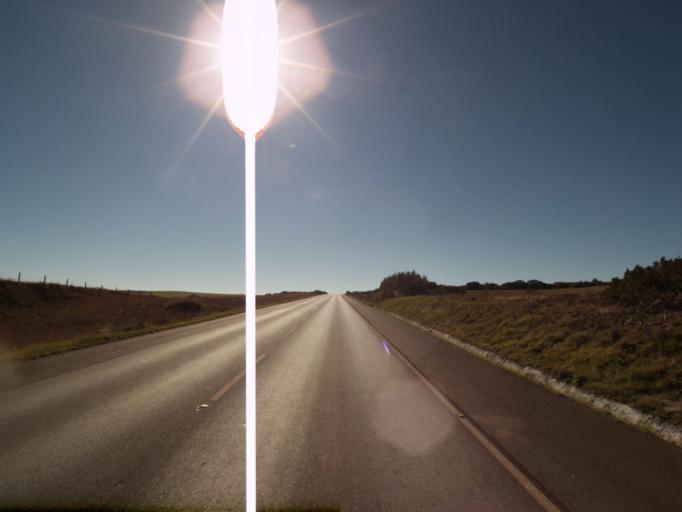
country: BR
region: Parana
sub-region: Palmas
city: Palmas
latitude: -26.7388
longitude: -51.6520
